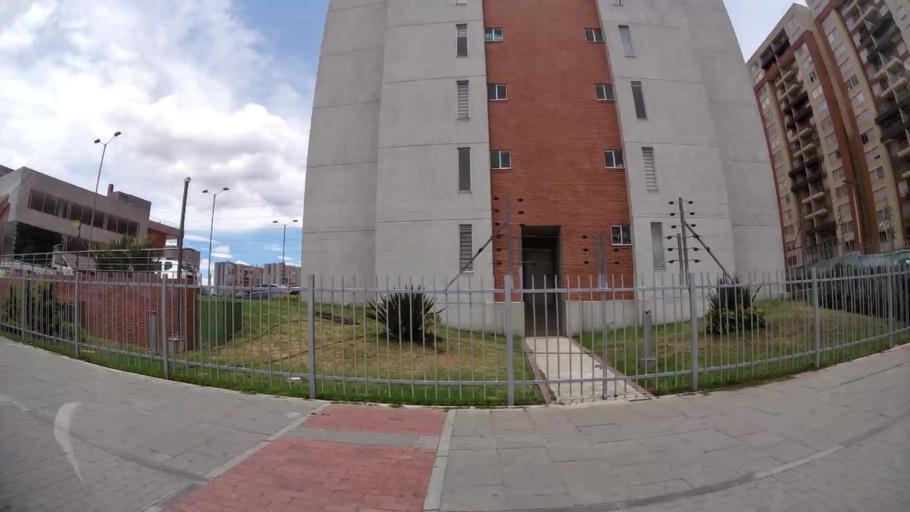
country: CO
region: Bogota D.C.
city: Bogota
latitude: 4.6413
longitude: -74.1452
